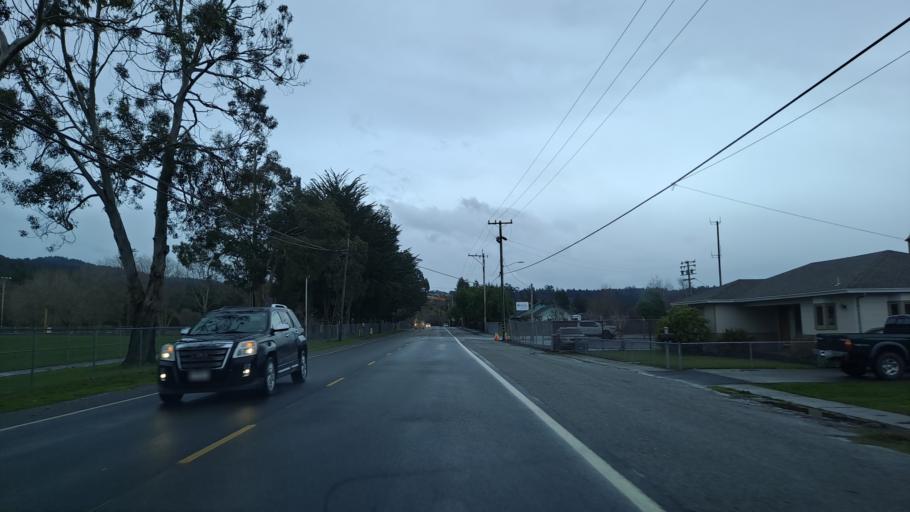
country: US
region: California
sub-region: Humboldt County
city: Fortuna
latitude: 40.5919
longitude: -124.1383
